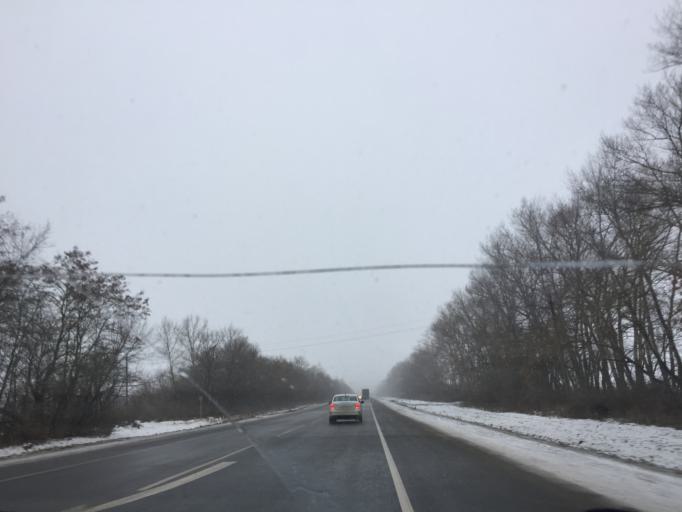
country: RU
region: Tula
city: Plavsk
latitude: 53.8025
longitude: 37.3817
